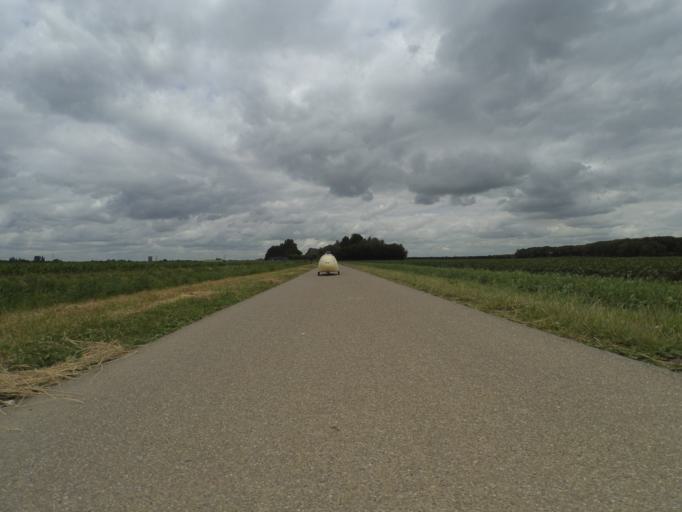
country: NL
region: South Holland
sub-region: Gemeente Dordrecht
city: Dordrecht
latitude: 51.7516
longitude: 4.6543
